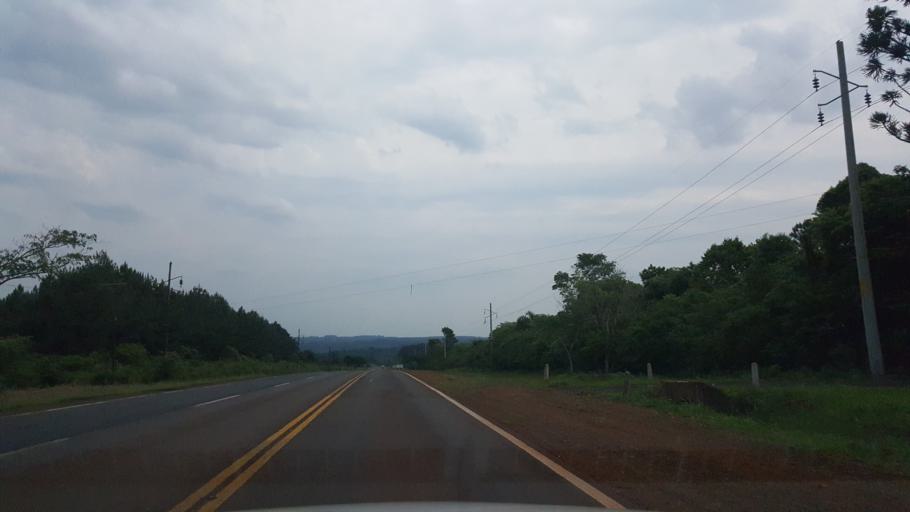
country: AR
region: Misiones
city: Capiovi
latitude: -26.9481
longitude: -55.0890
